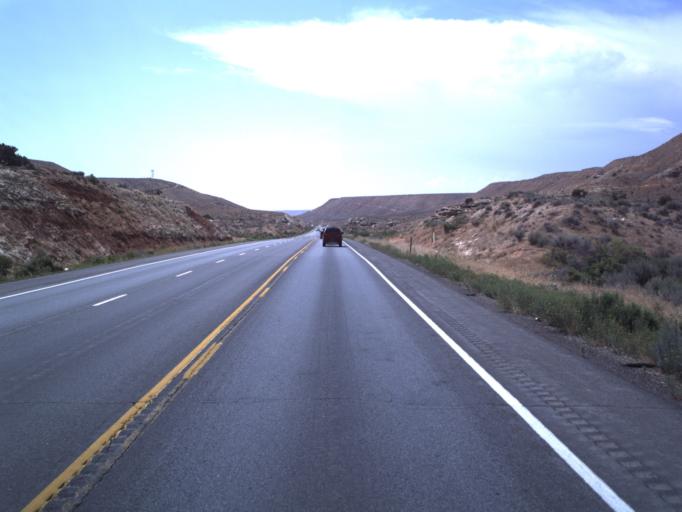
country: US
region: Utah
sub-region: Uintah County
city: Maeser
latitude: 40.3753
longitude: -109.6079
